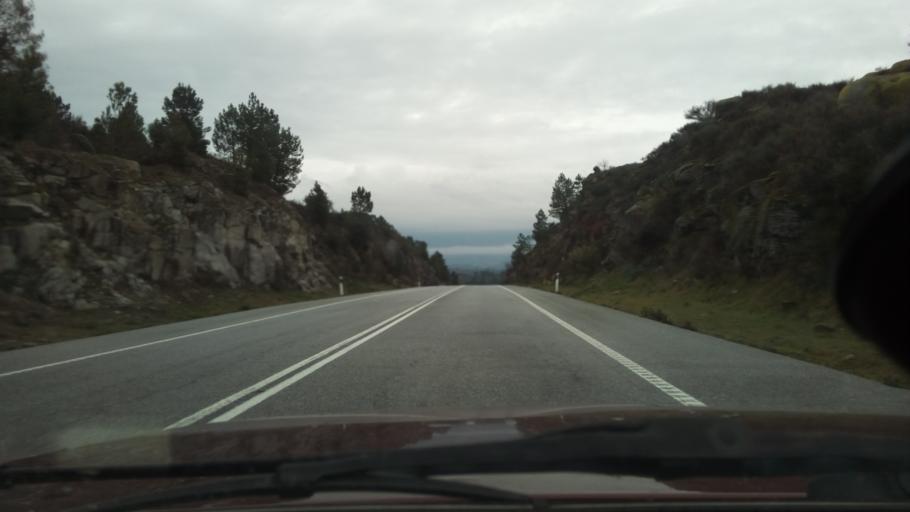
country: PT
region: Guarda
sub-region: Fornos de Algodres
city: Fornos de Algodres
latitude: 40.6052
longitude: -7.5862
